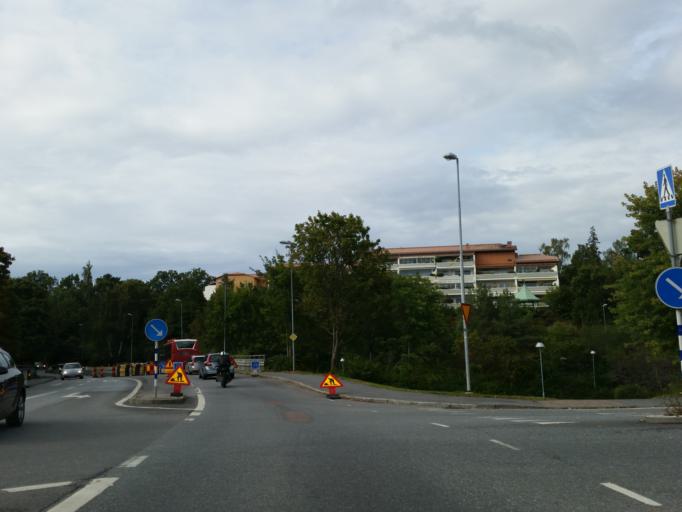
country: SE
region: Stockholm
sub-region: Sollentuna Kommun
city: Sollentuna
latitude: 59.4411
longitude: 17.9502
